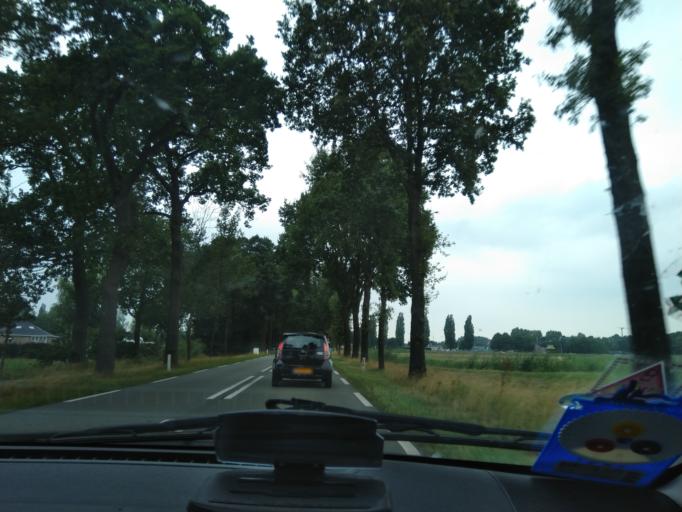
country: NL
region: Groningen
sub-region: Gemeente Pekela
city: Oude Pekela
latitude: 53.1107
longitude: 7.0312
